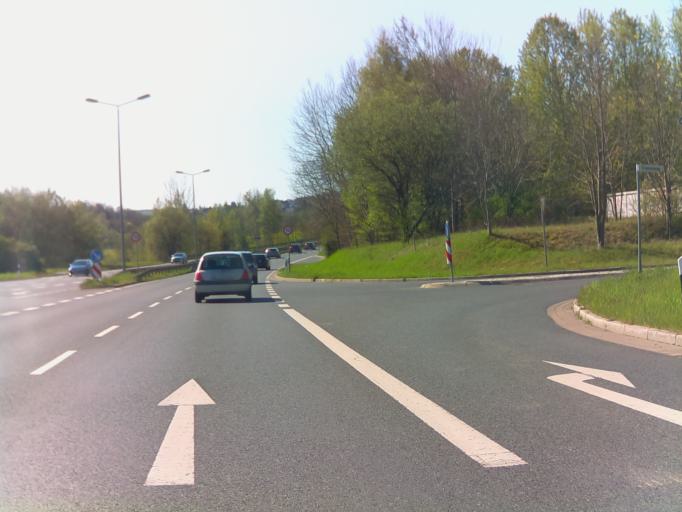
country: DE
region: Saxony
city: Plauen
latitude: 50.5039
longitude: 12.1705
